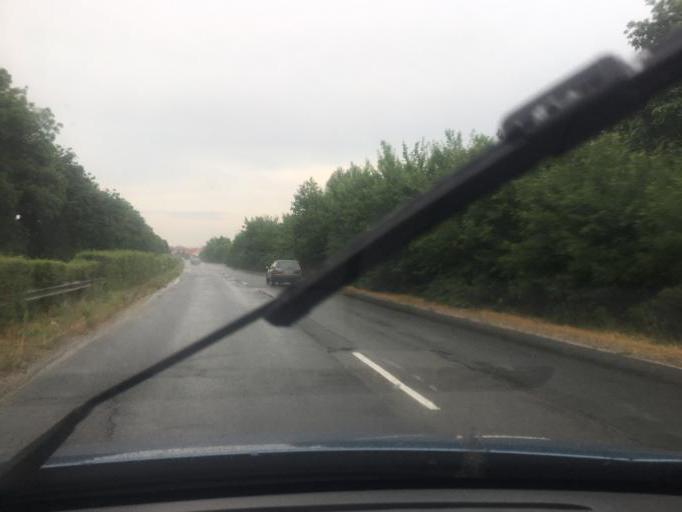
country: BG
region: Burgas
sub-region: Obshtina Burgas
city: Burgas
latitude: 42.5553
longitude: 27.5118
